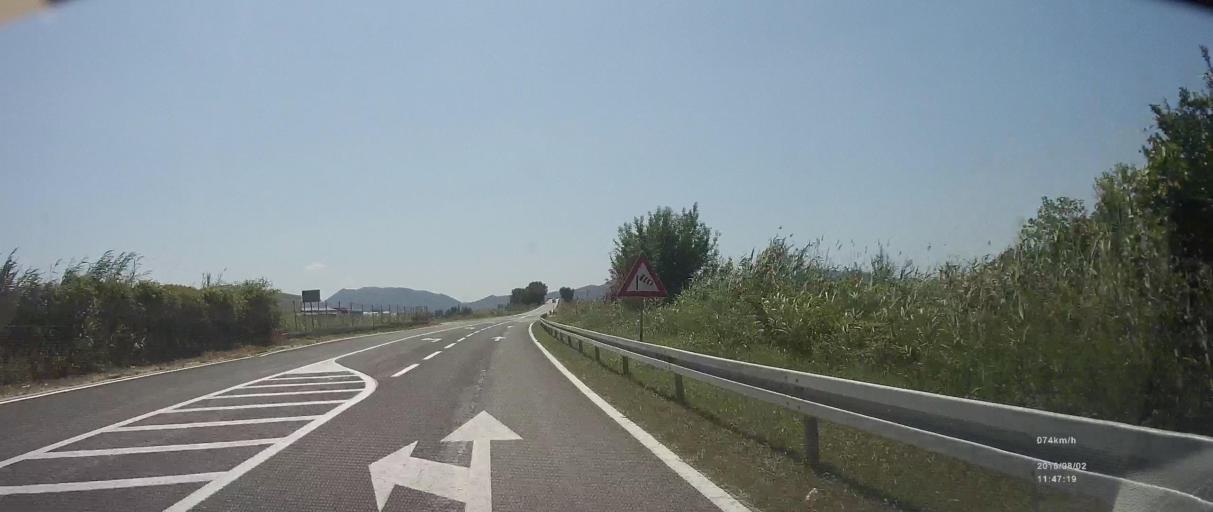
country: HR
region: Dubrovacko-Neretvanska
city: Komin
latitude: 43.0451
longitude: 17.4814
